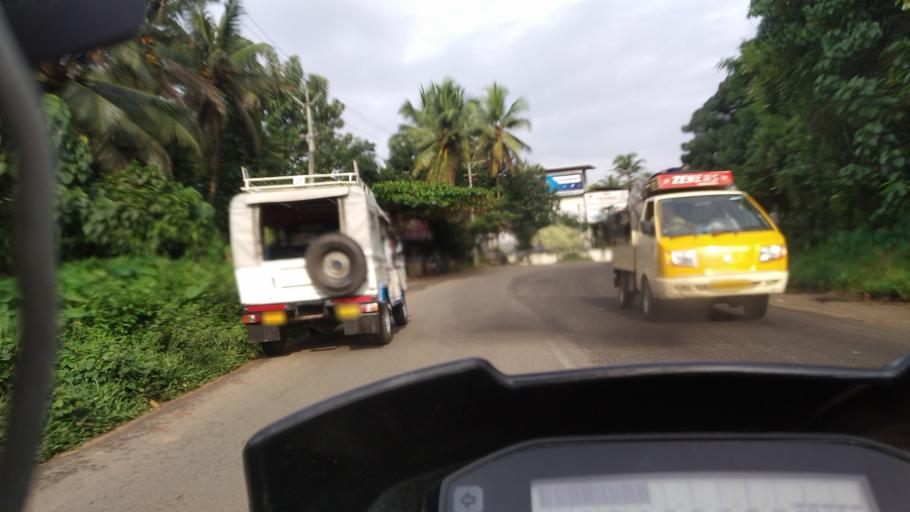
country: IN
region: Kerala
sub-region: Ernakulam
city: Kotamangalam
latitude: 10.0516
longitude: 76.7134
